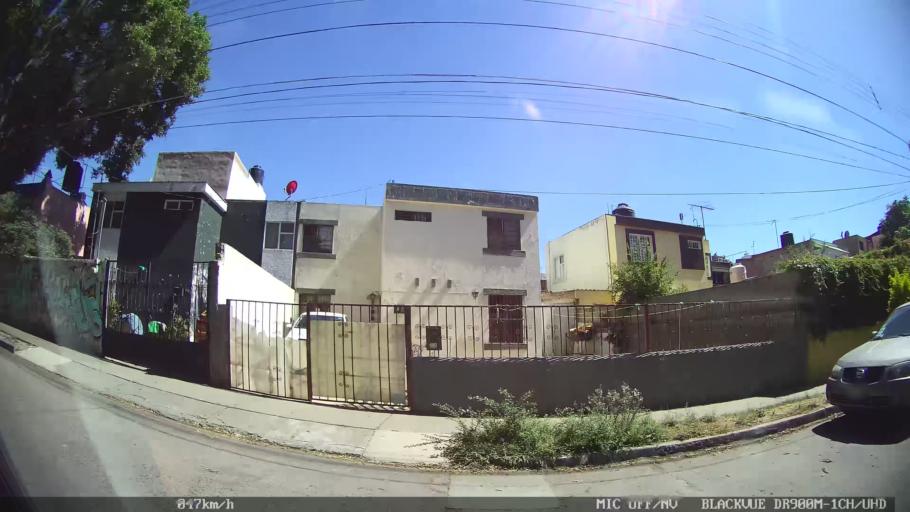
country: MX
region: Jalisco
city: Tlaquepaque
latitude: 20.6487
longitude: -103.2961
